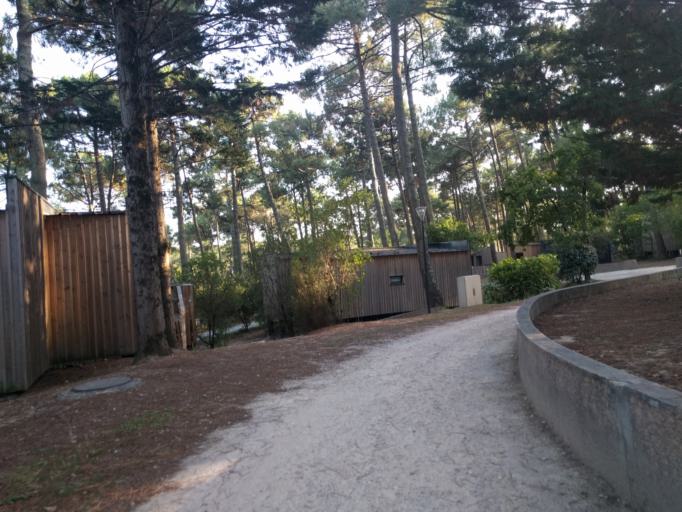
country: FR
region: Aquitaine
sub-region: Departement de la Gironde
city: Ares
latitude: 44.7533
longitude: -1.1877
